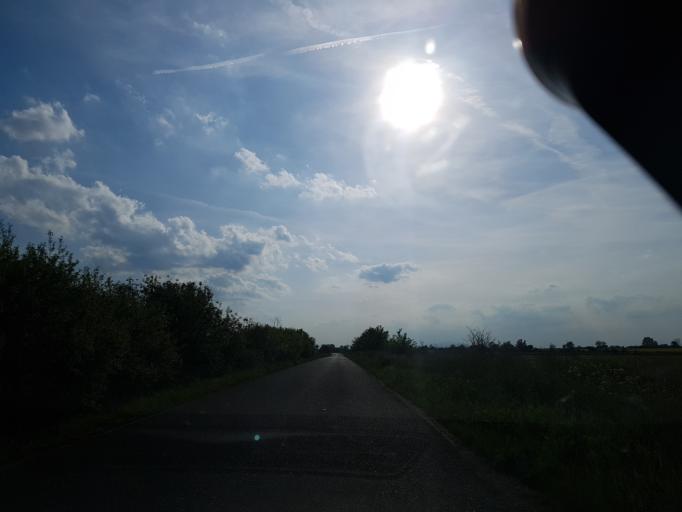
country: PL
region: Lower Silesian Voivodeship
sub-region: Powiat strzelinski
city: Wiazow
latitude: 50.8395
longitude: 17.1934
